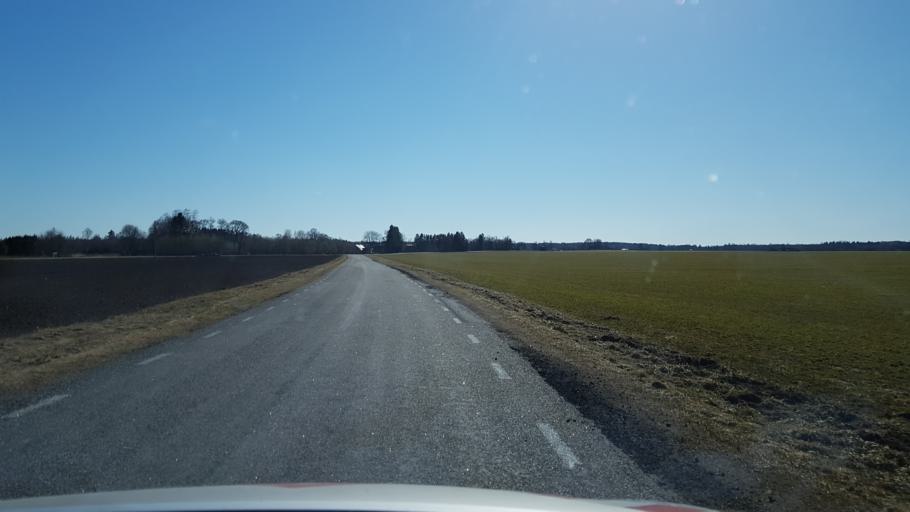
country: EE
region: Laeaene-Virumaa
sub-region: Viru-Nigula vald
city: Kunda
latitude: 59.4024
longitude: 26.5151
